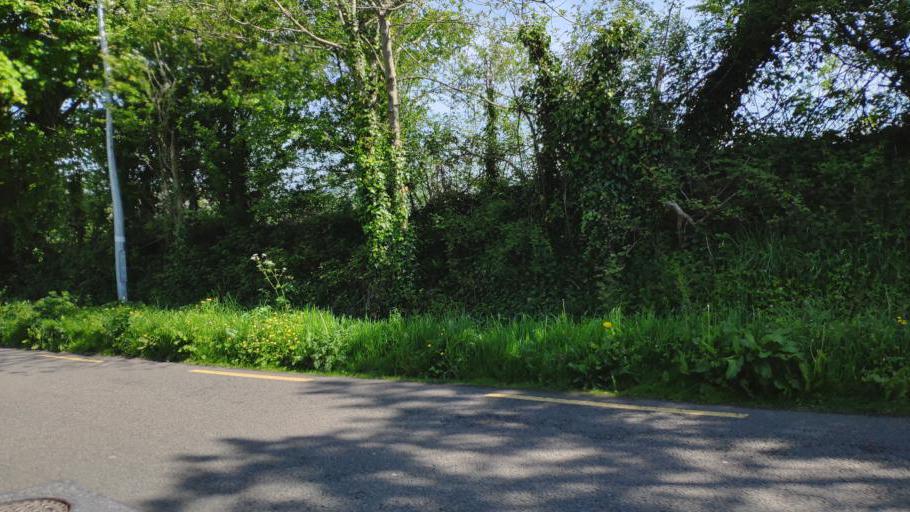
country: IE
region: Munster
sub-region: County Cork
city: Blarney
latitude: 51.9236
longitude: -8.5540
